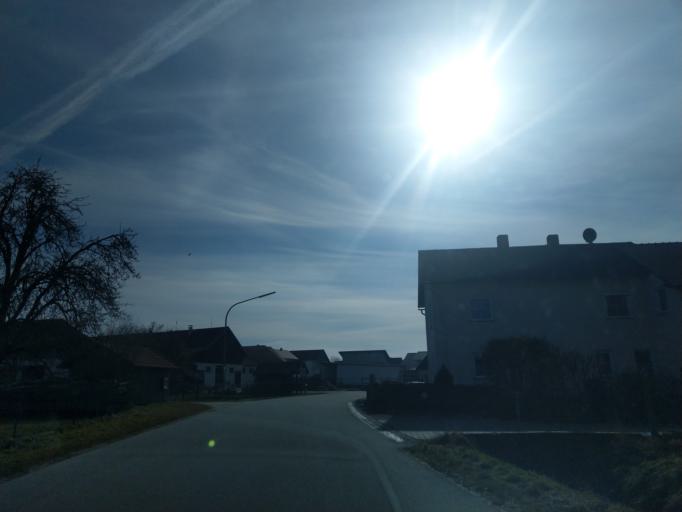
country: DE
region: Bavaria
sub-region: Lower Bavaria
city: Buchhofen
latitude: 48.6704
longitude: 12.9638
